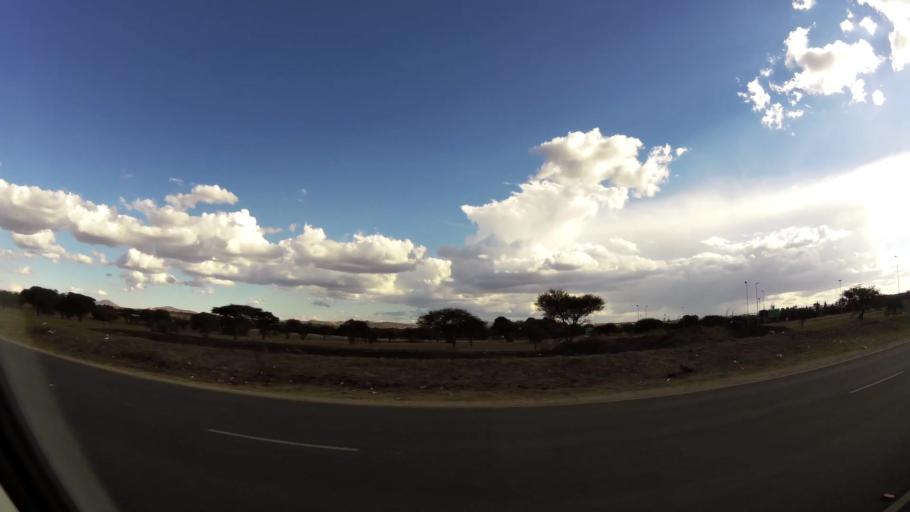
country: ZA
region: Limpopo
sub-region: Capricorn District Municipality
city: Polokwane
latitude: -23.9277
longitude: 29.4689
